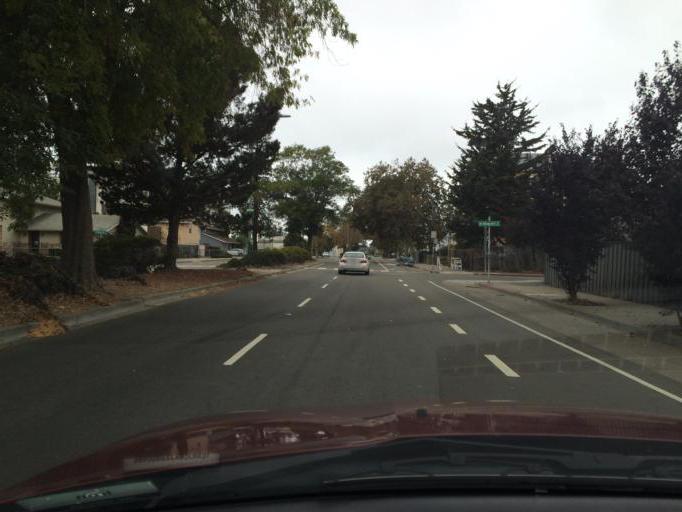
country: US
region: California
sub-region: Alameda County
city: Oakland
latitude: 37.8097
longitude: -122.2867
